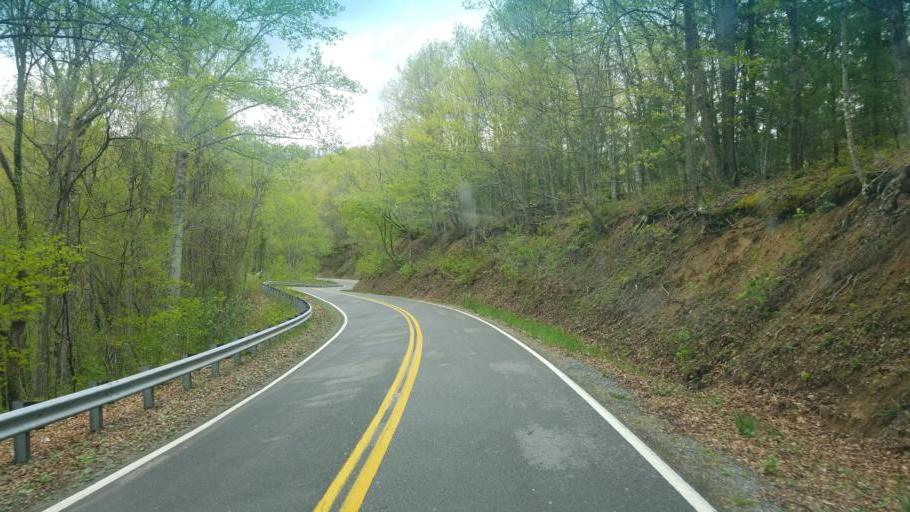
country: US
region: Virginia
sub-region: Tazewell County
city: Tazewell
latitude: 37.0112
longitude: -81.5201
